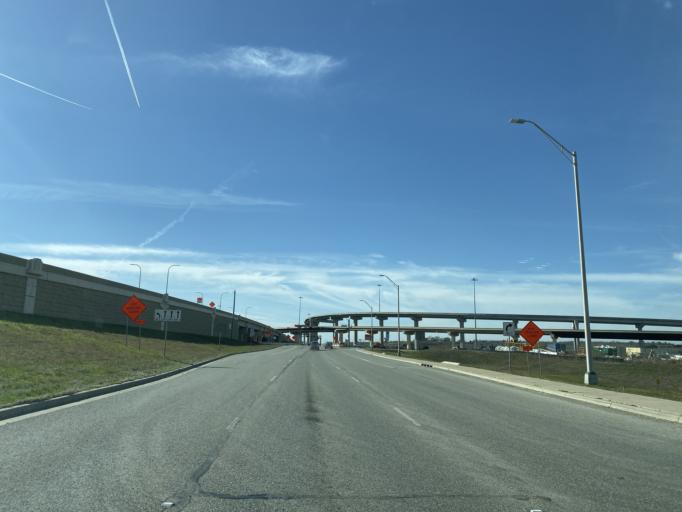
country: US
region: Texas
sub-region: Travis County
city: Manor
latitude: 30.3418
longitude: -97.5890
